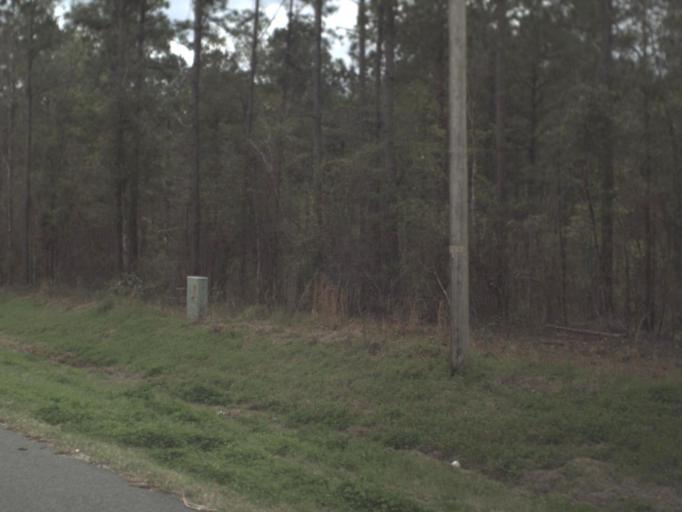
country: US
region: Florida
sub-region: Gadsden County
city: Quincy
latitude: 30.5108
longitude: -84.6096
